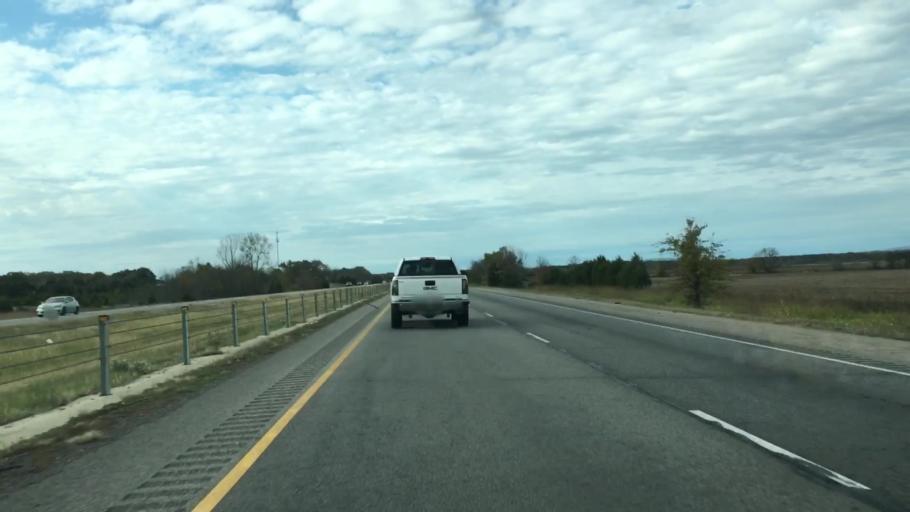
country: US
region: Arkansas
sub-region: Conway County
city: Morrilton
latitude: 35.1974
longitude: -92.8020
